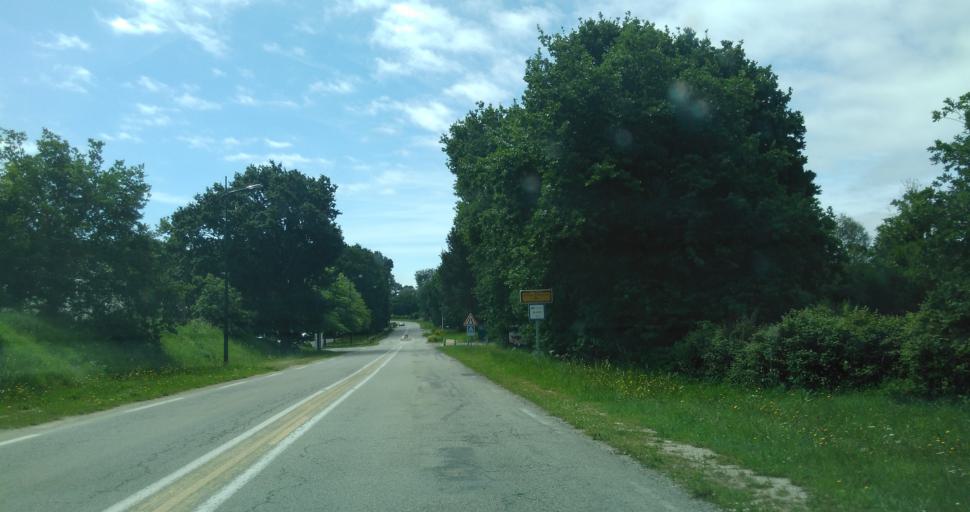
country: FR
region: Brittany
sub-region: Departement du Morbihan
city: La Trinite-sur-Mer
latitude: 47.5937
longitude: -3.0360
